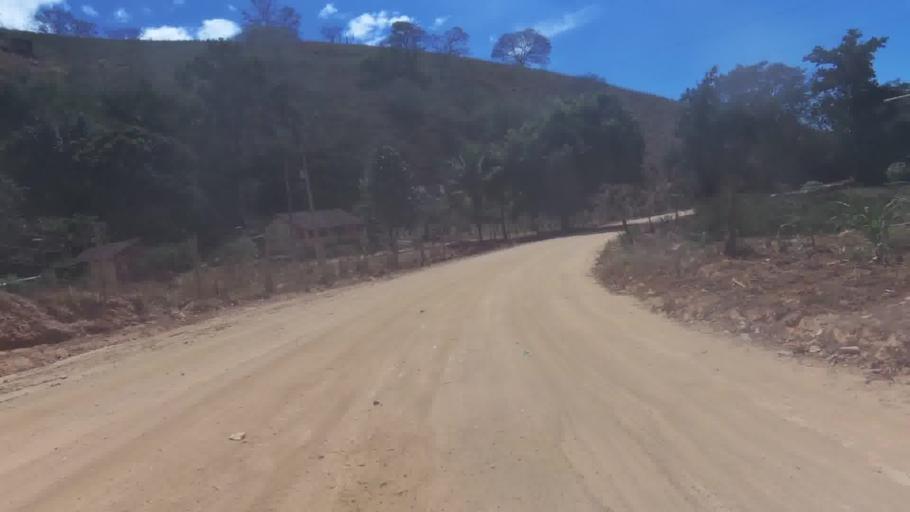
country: BR
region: Espirito Santo
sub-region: Cachoeiro De Itapemirim
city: Cachoeiro de Itapemirim
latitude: -20.9430
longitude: -41.2241
